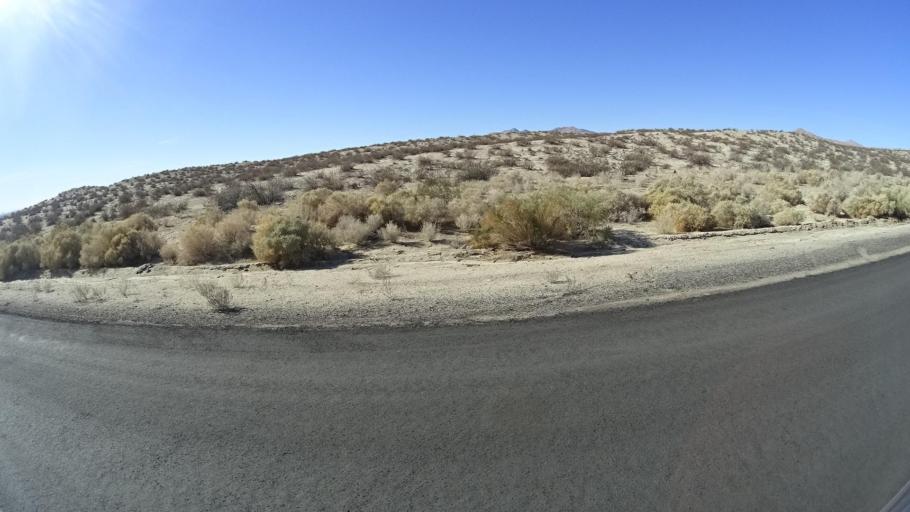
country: US
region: California
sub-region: Kern County
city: California City
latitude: 35.3219
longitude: -117.9623
